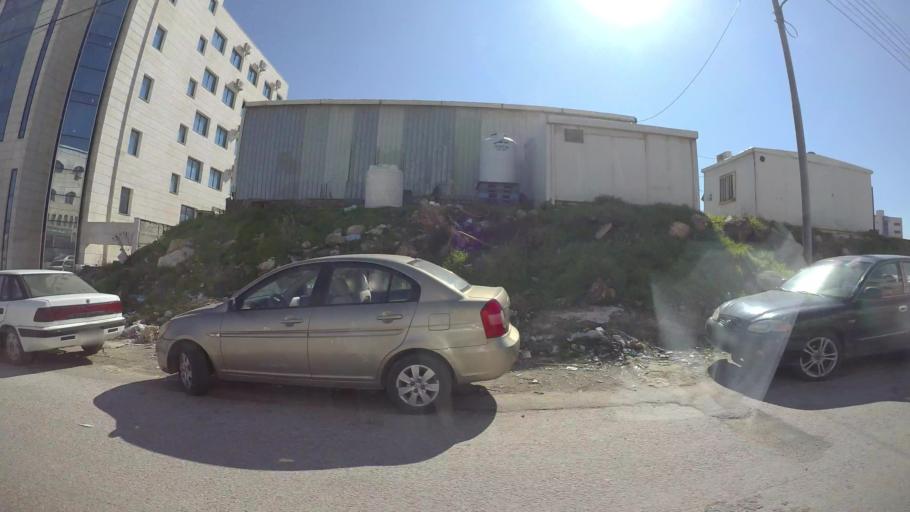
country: JO
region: Amman
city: Al Bunayyat ash Shamaliyah
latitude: 31.9154
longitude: 35.9087
